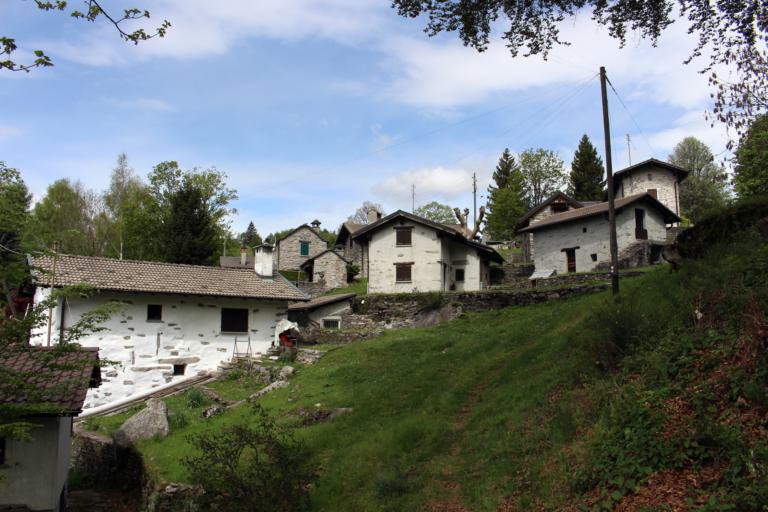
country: CH
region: Ticino
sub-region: Locarno District
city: Gordola
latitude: 46.1972
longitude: 8.8680
